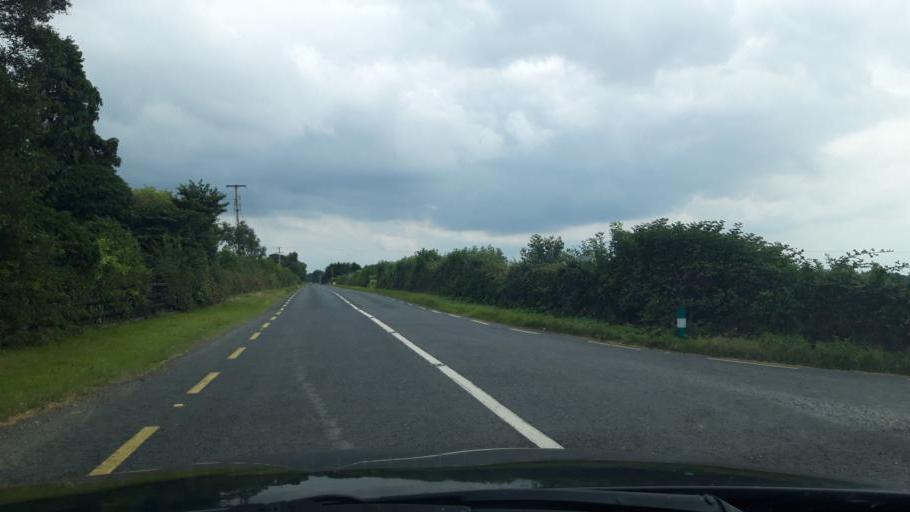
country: IE
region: Leinster
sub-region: Kildare
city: Athy
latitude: 53.0220
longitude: -7.0064
